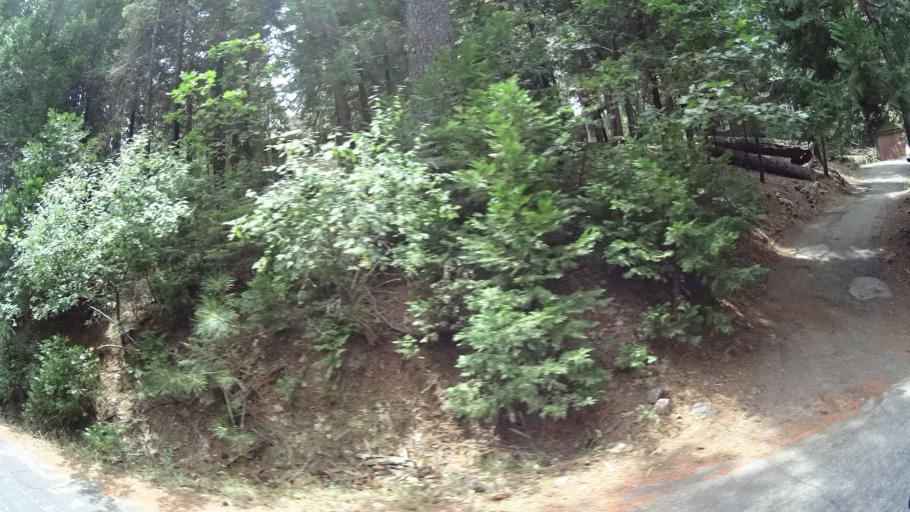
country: US
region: California
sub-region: Calaveras County
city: Arnold
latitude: 38.2519
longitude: -120.3454
